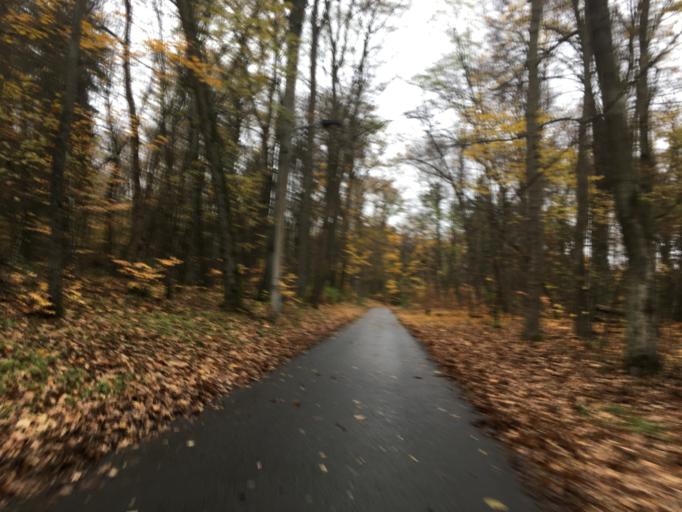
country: DE
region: Brandenburg
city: Gross Lindow
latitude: 52.2828
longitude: 14.5141
